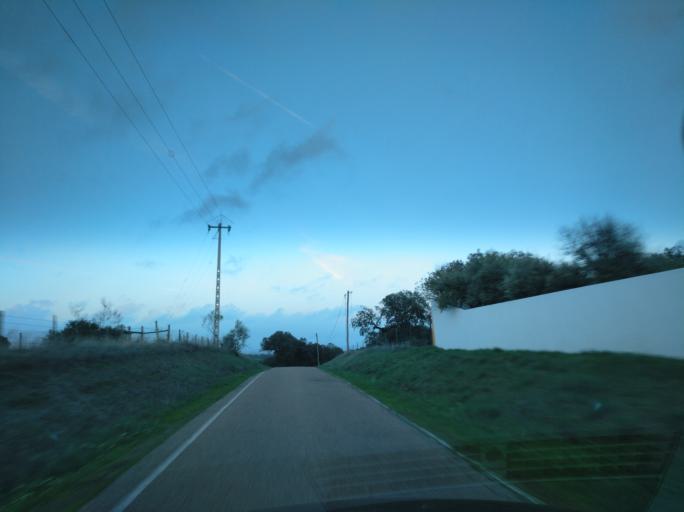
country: PT
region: Portalegre
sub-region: Campo Maior
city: Campo Maior
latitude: 39.0702
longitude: -7.1162
